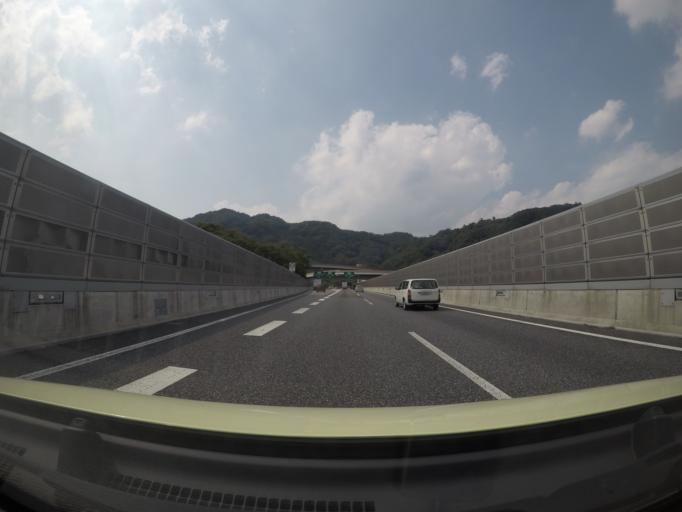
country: JP
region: Tokyo
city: Hachioji
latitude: 35.6386
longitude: 139.2557
